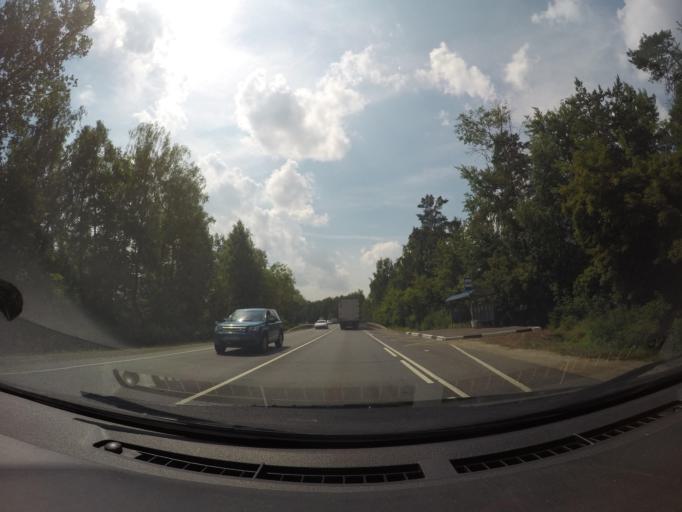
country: RU
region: Moskovskaya
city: Malyshevo
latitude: 55.4912
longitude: 38.3457
